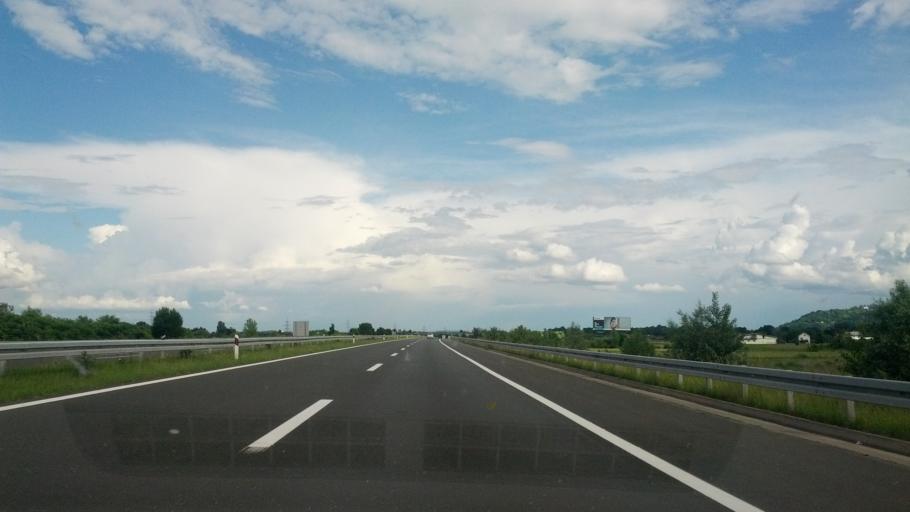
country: HR
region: Zagrebacka
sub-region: Grad Samobor
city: Samobor
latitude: 45.8222
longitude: 15.7473
